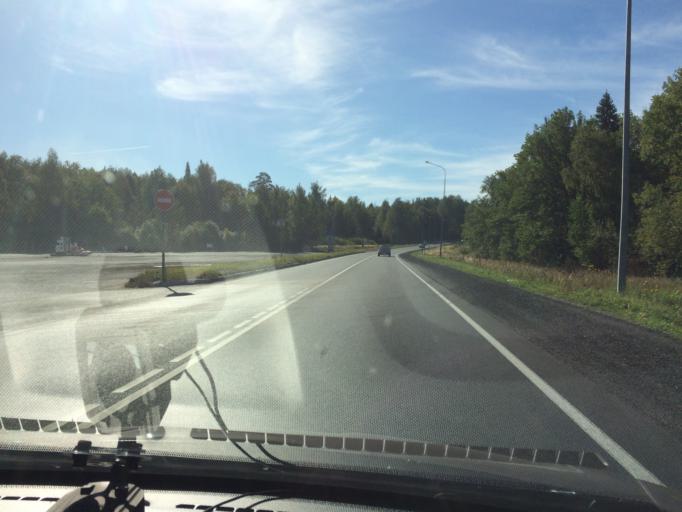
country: RU
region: Mariy-El
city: Yoshkar-Ola
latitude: 56.5971
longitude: 47.9731
